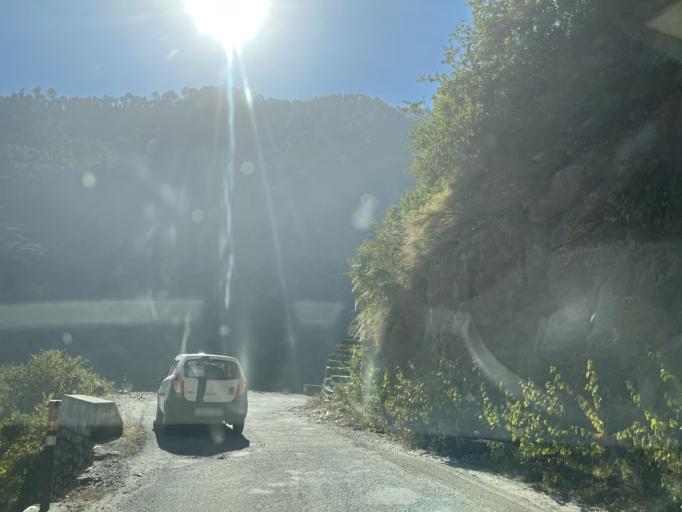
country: IN
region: Uttarakhand
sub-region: Naini Tal
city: Naini Tal
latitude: 29.5095
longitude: 79.4654
